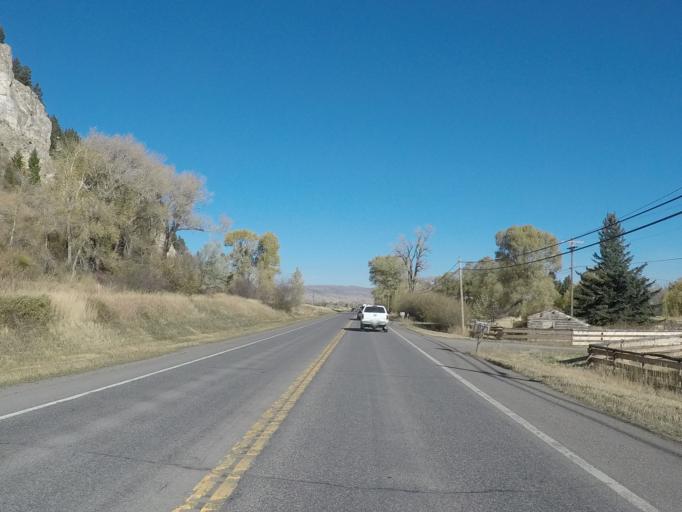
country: US
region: Montana
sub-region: Park County
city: Livingston
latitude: 45.6102
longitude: -110.5768
